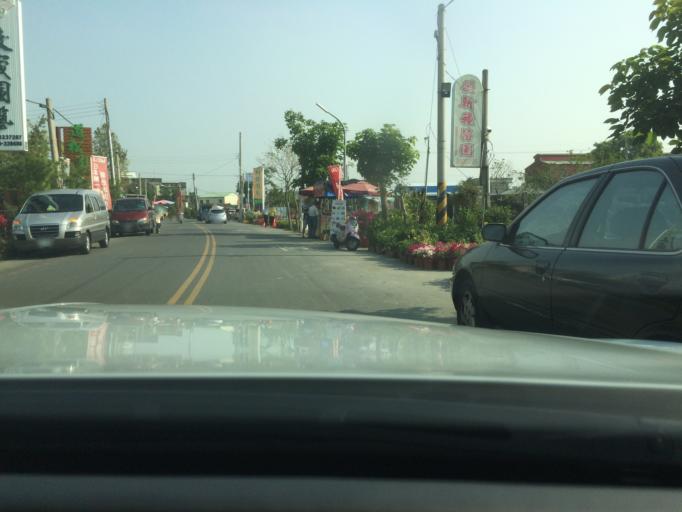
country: TW
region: Taiwan
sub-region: Nantou
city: Nantou
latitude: 23.9014
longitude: 120.5266
